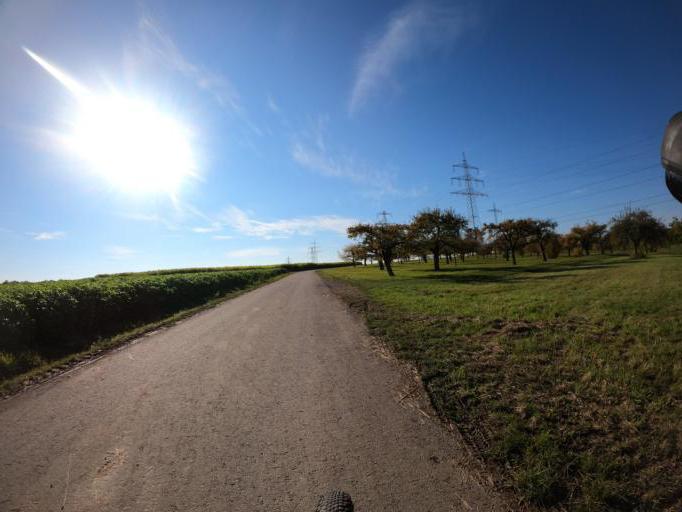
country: DE
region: Baden-Wuerttemberg
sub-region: Regierungsbezirk Stuttgart
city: Magstadt
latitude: 48.7368
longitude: 8.9546
